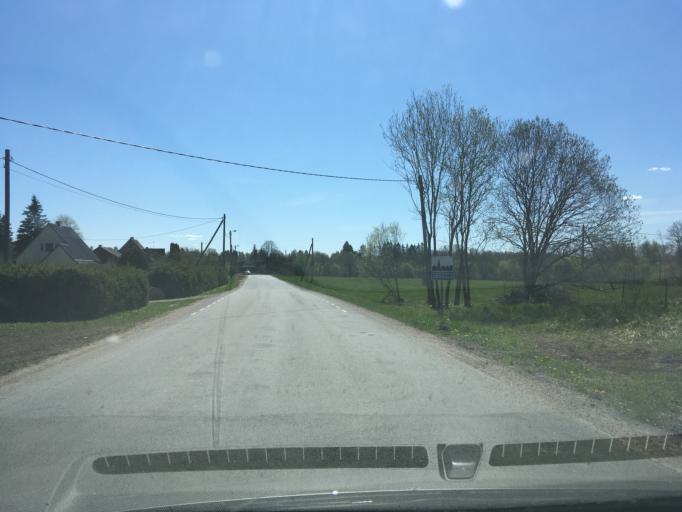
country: EE
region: Harju
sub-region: Raasiku vald
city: Arukula
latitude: 59.3761
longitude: 25.0769
